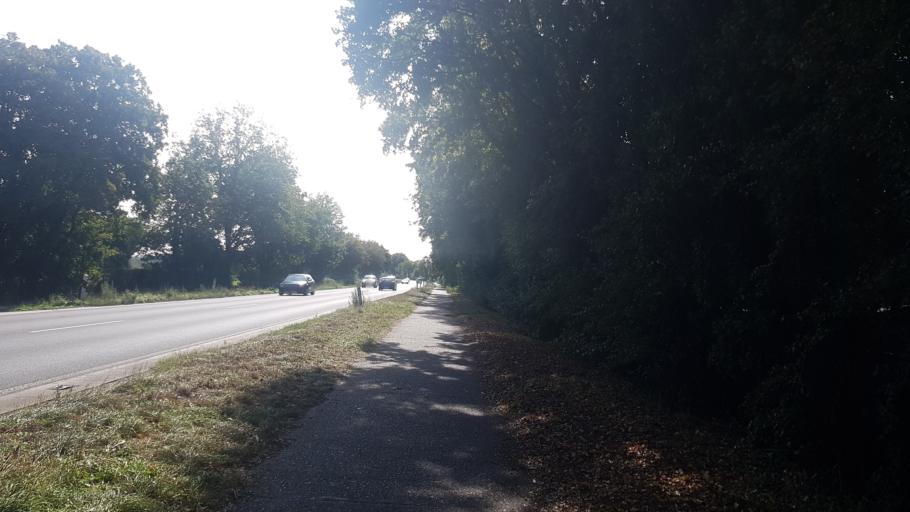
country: DE
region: North Rhine-Westphalia
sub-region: Regierungsbezirk Dusseldorf
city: Ratingen
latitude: 51.3181
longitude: 6.8314
